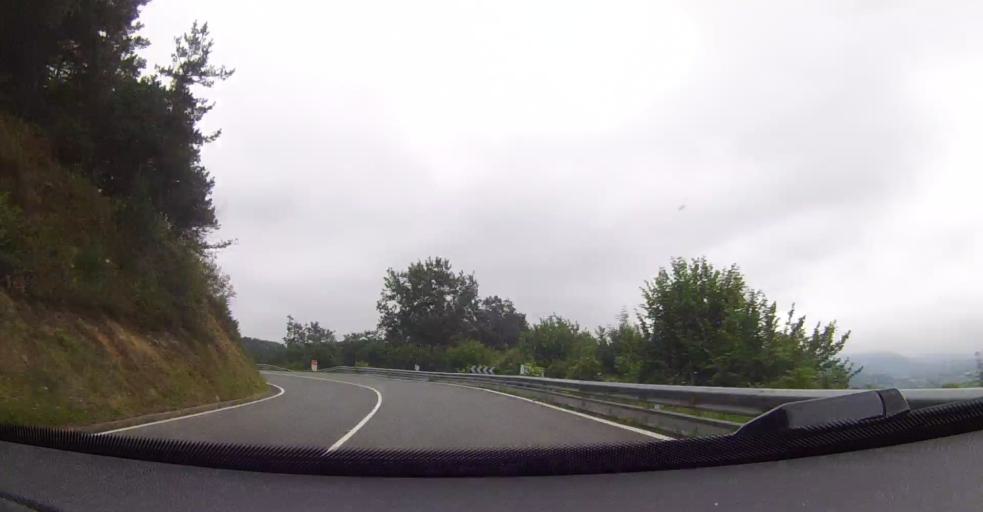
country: ES
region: Basque Country
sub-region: Bizkaia
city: Balmaseda
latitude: 43.2430
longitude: -3.2993
